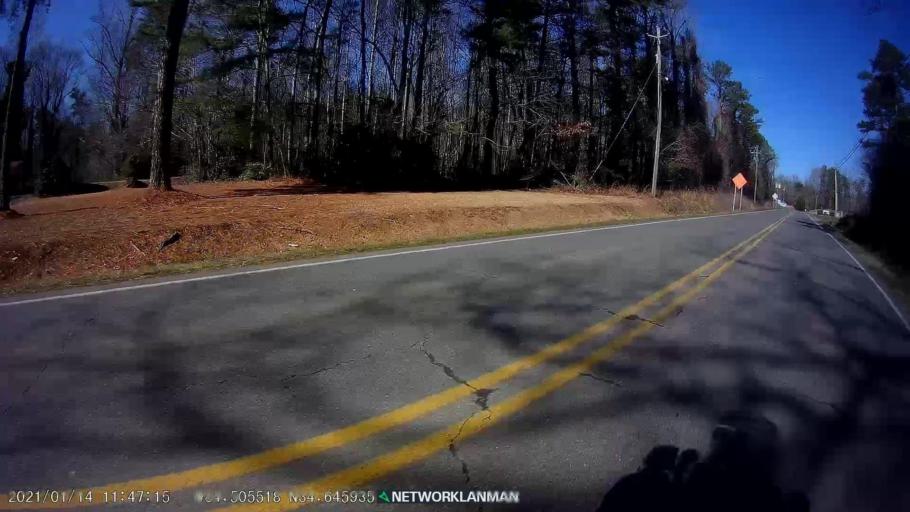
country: US
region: Georgia
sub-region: Gilmer County
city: Ellijay
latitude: 34.6463
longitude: -84.5062
